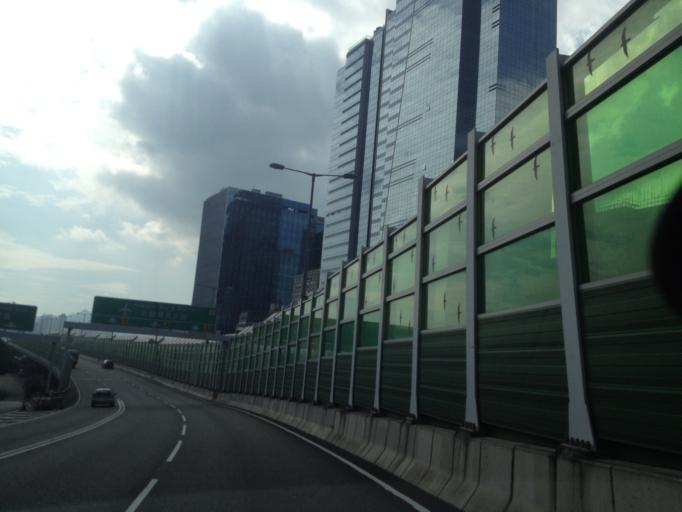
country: HK
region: Kowloon City
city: Kowloon
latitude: 22.3086
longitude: 114.2275
